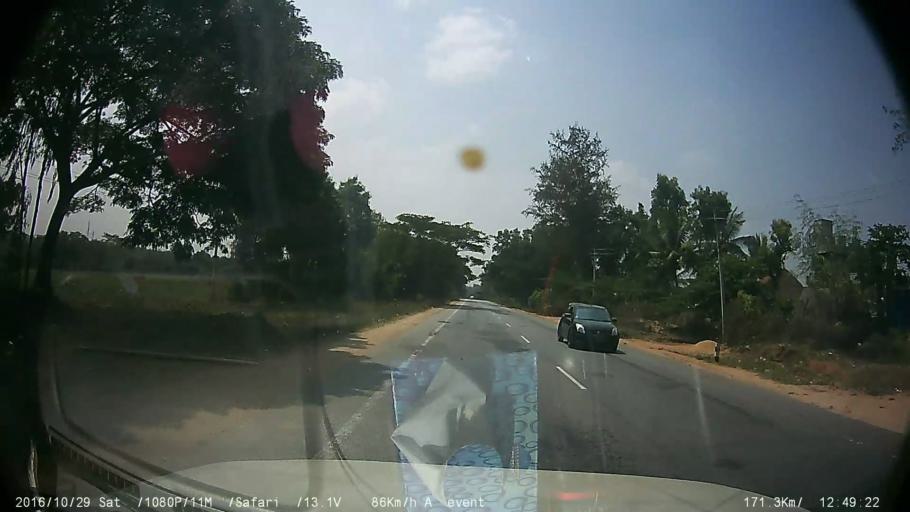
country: IN
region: Karnataka
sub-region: Mysore
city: Hunsur
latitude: 12.3281
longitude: 76.3640
